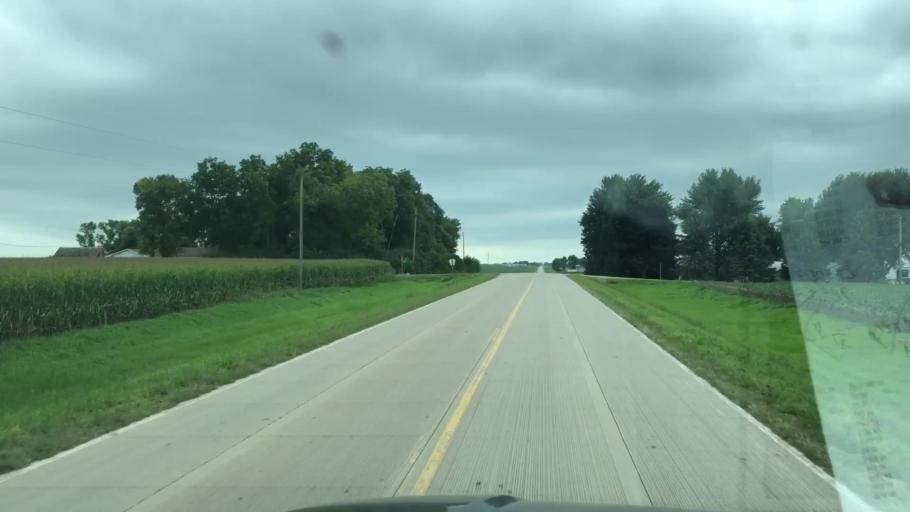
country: US
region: Iowa
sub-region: O'Brien County
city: Sheldon
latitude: 43.1432
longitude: -95.9795
